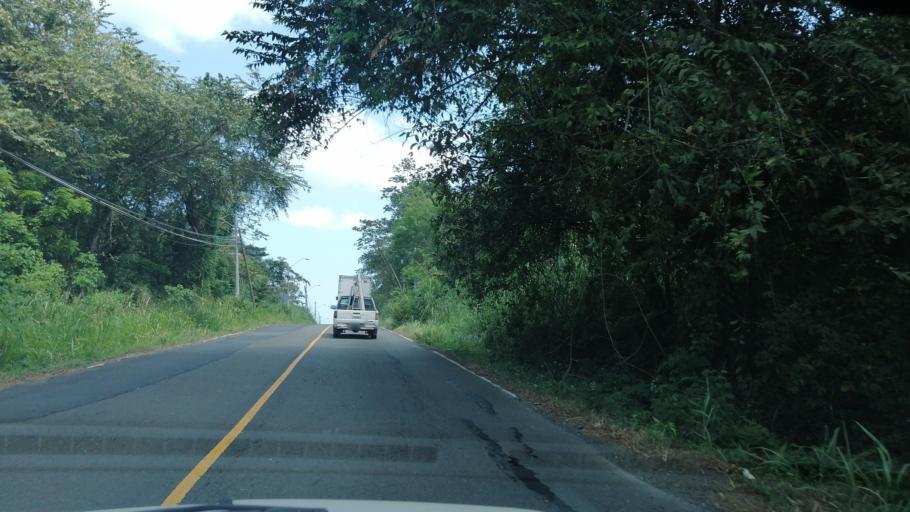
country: PA
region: Panama
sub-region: Distrito de Panama
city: Ancon
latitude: 8.9210
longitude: -79.5662
